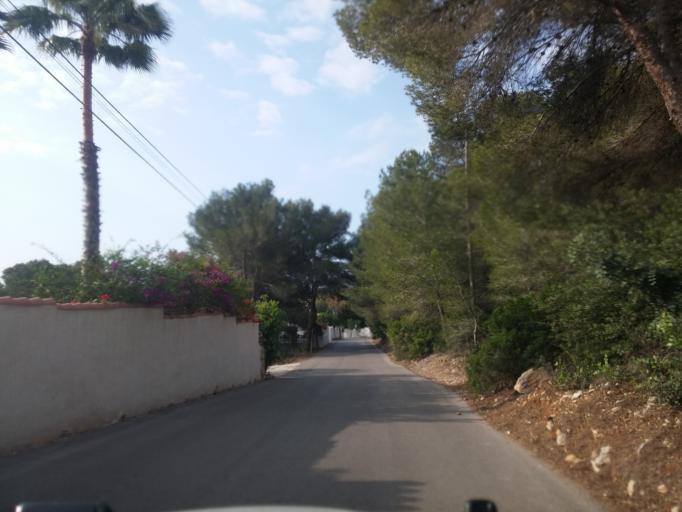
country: ES
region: Valencia
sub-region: Provincia de Alicante
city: Moraira
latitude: 38.6963
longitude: 0.1403
